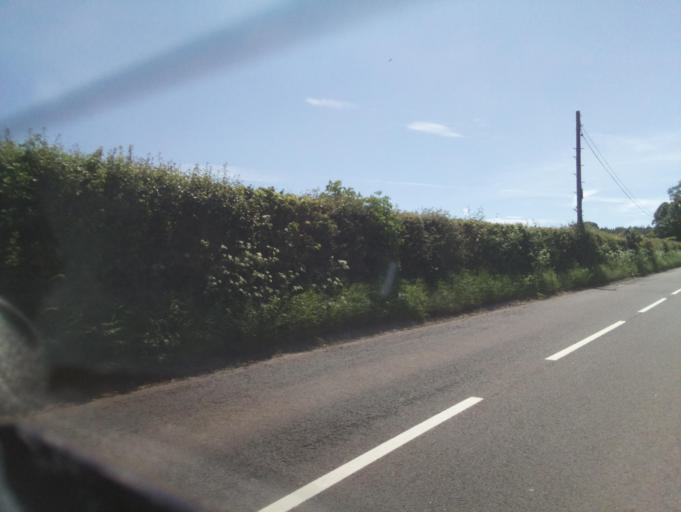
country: GB
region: Wales
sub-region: Monmouthshire
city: Mitchel Troy
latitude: 51.7248
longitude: -2.7572
